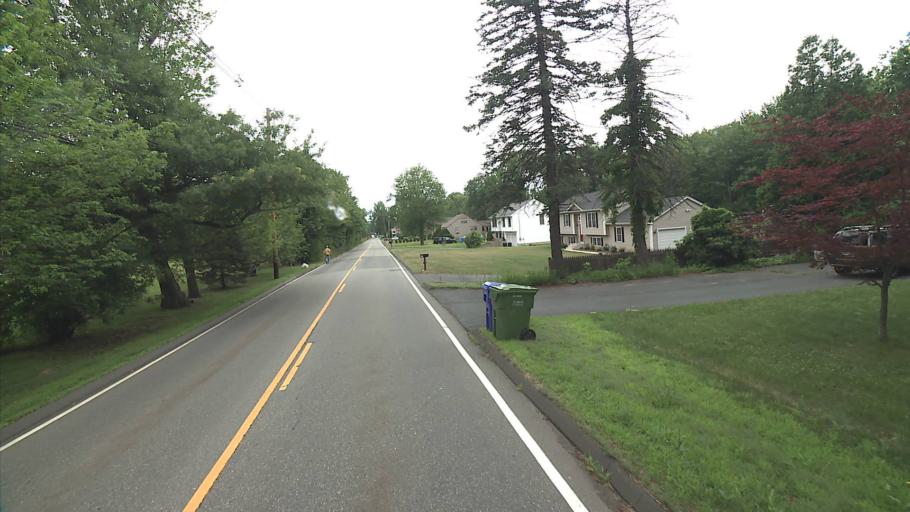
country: US
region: Connecticut
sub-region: New Haven County
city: Wallingford Center
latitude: 41.4435
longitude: -72.8045
